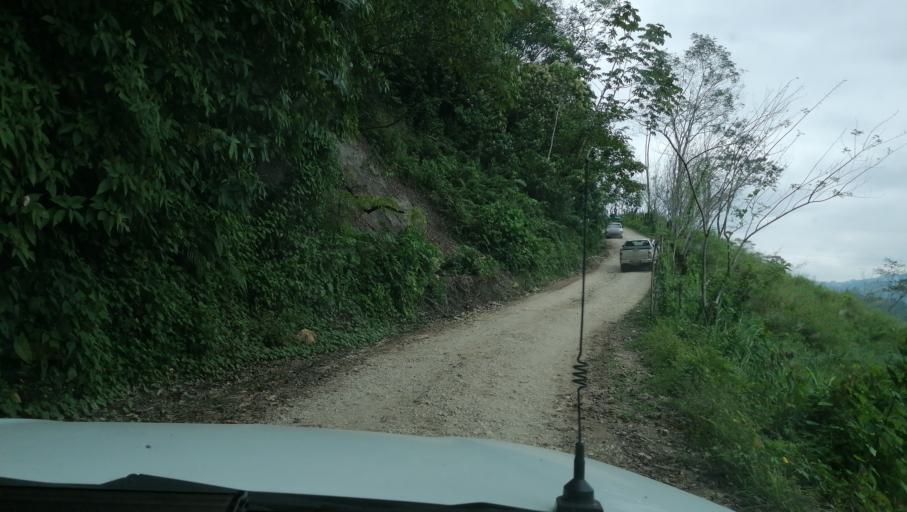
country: MX
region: Chiapas
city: Ocotepec
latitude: 17.2775
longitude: -93.2264
